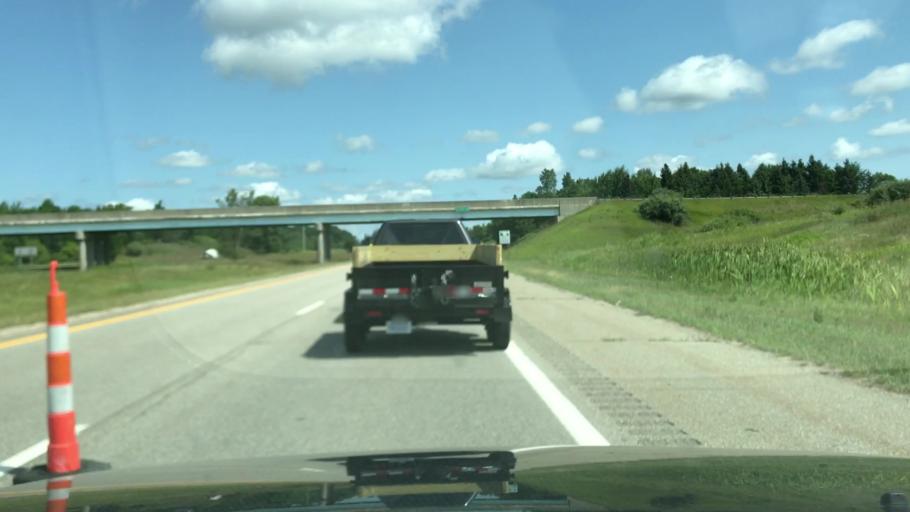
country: US
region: Michigan
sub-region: Mecosta County
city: Big Rapids
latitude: 43.7706
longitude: -85.5345
